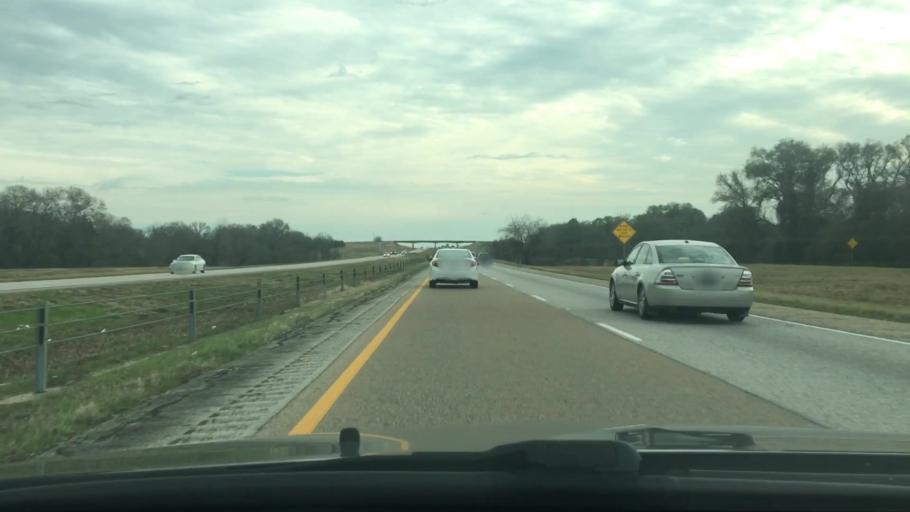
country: US
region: Texas
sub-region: Leon County
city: Centerville
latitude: 31.1310
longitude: -95.9782
